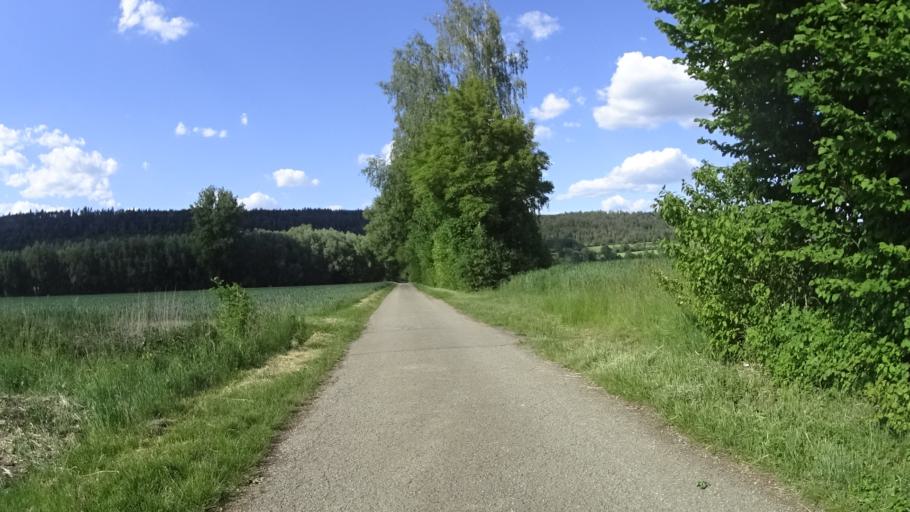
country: DE
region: Bavaria
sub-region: Upper Palatinate
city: Dietfurt
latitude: 49.0189
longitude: 11.4986
